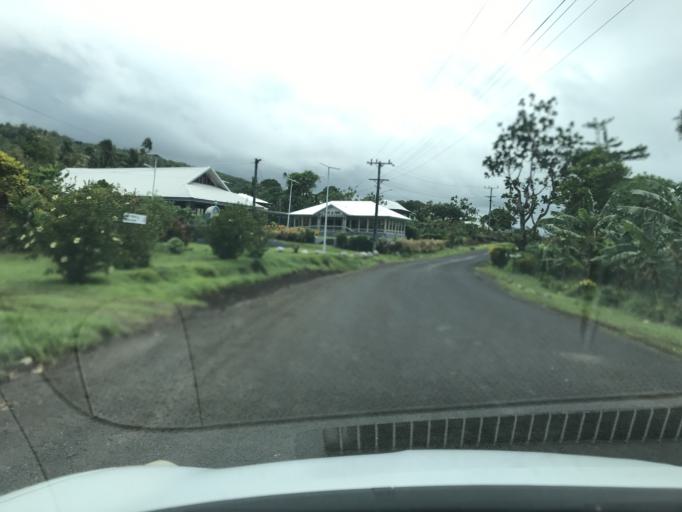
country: WS
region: Atua
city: Lufilufi
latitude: -13.8764
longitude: -171.6036
